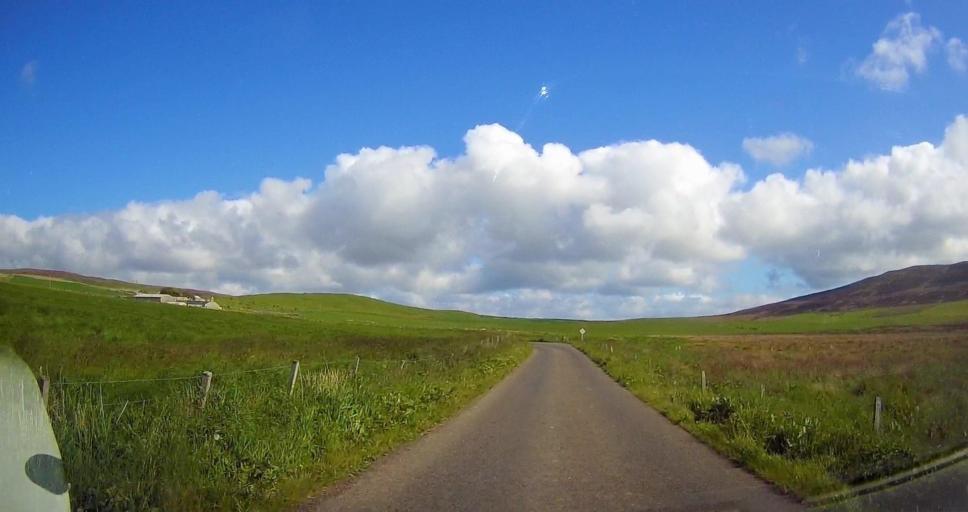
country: GB
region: Scotland
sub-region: Orkney Islands
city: Stromness
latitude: 58.9844
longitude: -3.1474
